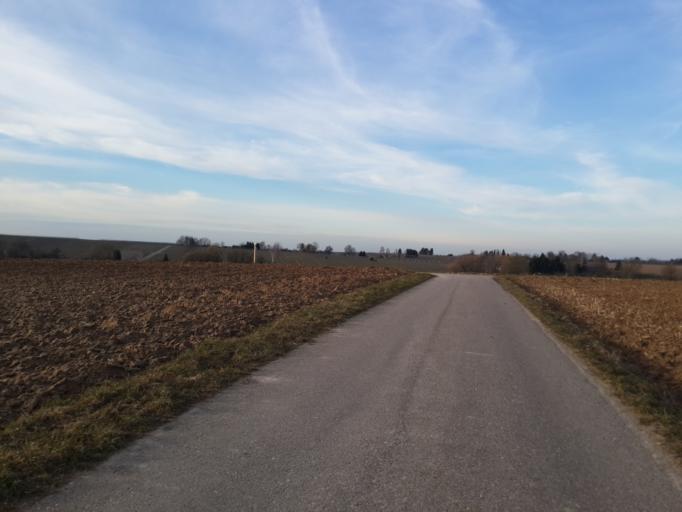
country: DE
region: Baden-Wuerttemberg
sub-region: Regierungsbezirk Stuttgart
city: Nordheim
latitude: 49.1246
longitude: 9.1227
